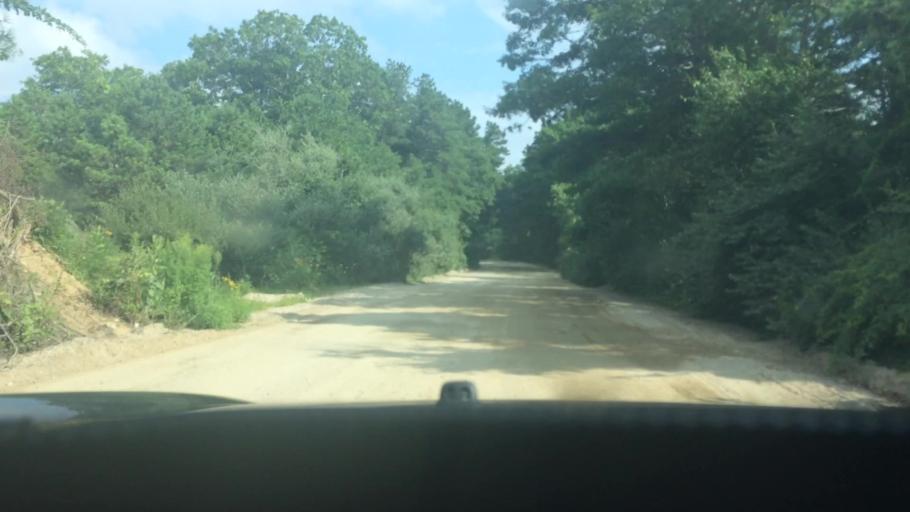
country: US
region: Massachusetts
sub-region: Barnstable County
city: Sandwich
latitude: 41.7245
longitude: -70.4860
